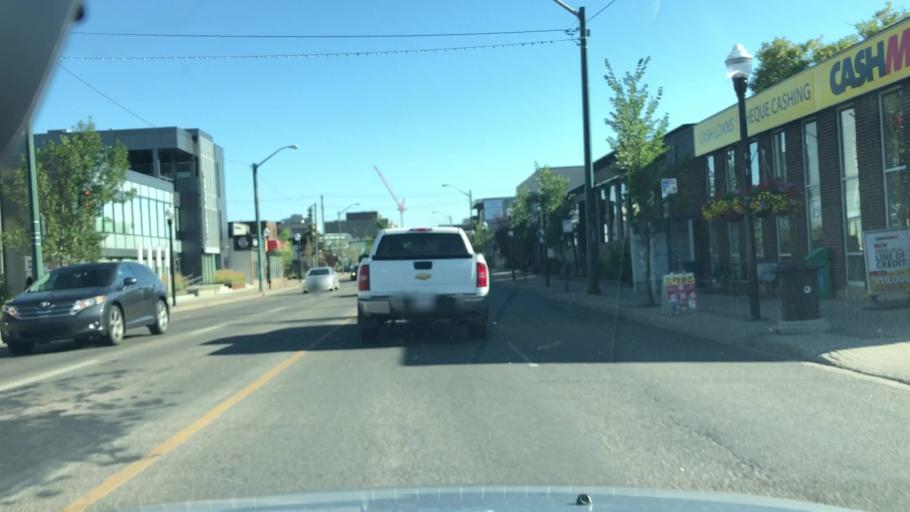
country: CA
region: Alberta
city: Edmonton
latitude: 53.5509
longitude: -113.5359
